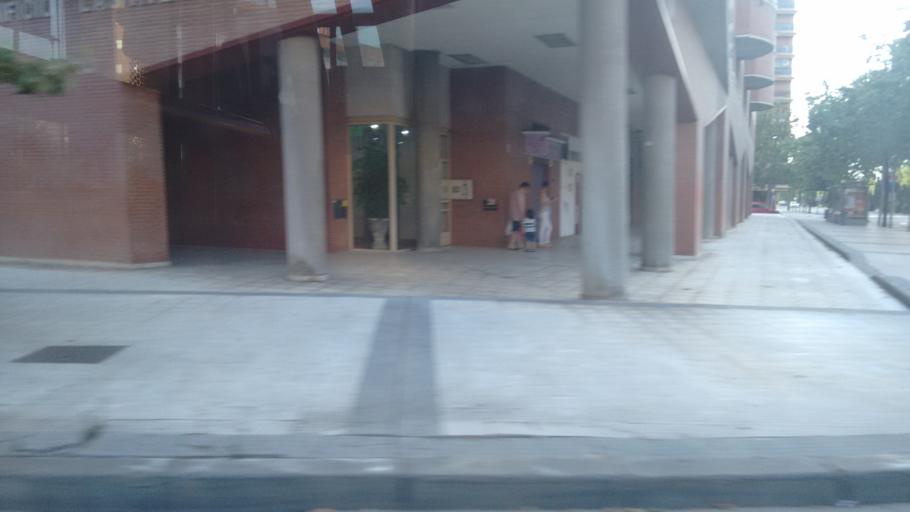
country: ES
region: Aragon
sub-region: Provincia de Zaragoza
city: Zaragoza
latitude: 41.6624
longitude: -0.8649
